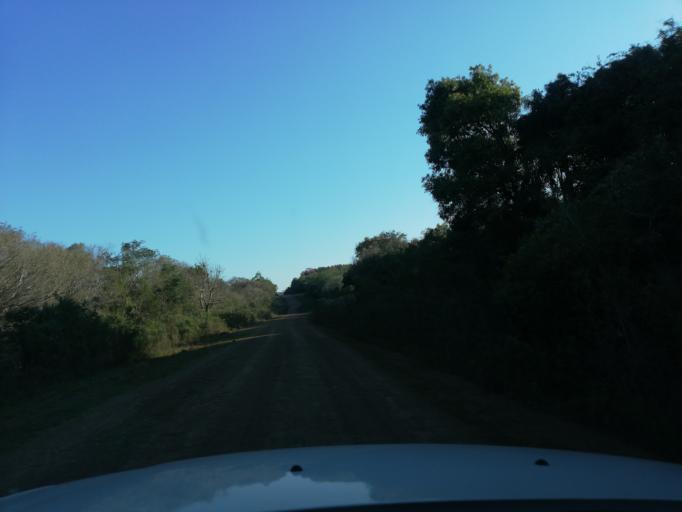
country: AR
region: Misiones
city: Cerro Cora
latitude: -27.5919
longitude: -55.6927
